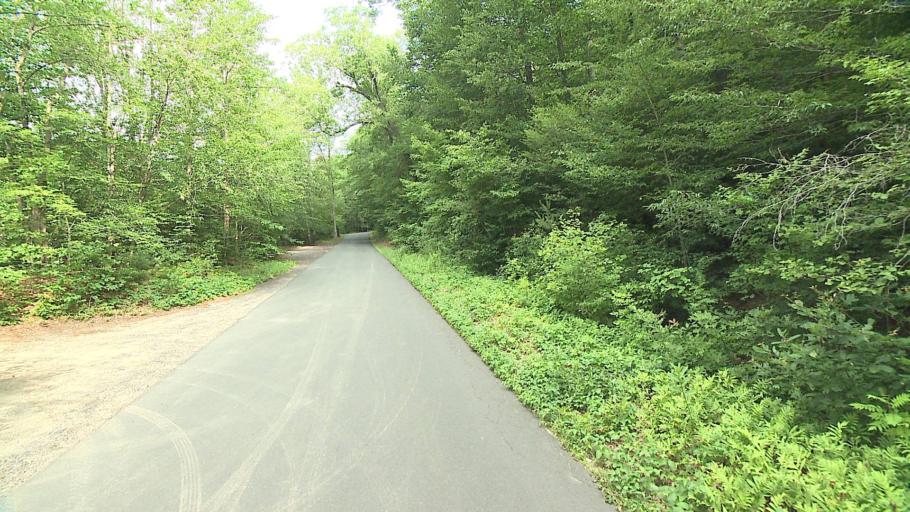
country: US
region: Connecticut
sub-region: Litchfield County
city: Winsted
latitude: 41.9395
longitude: -73.0037
